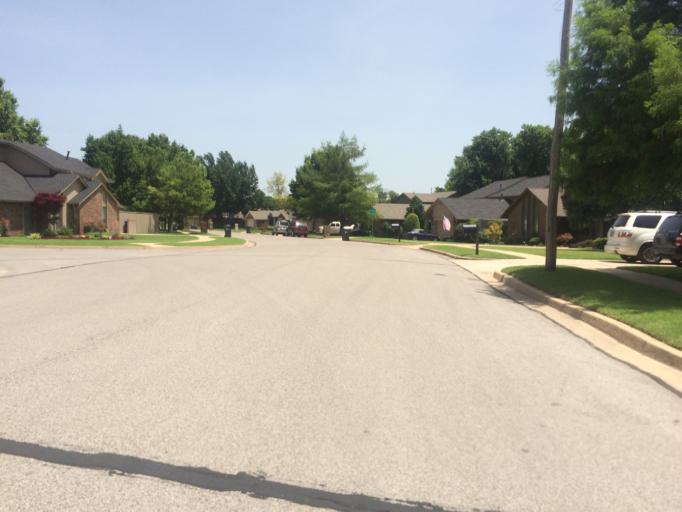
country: US
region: Oklahoma
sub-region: Cleveland County
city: Norman
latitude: 35.1867
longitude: -97.4659
